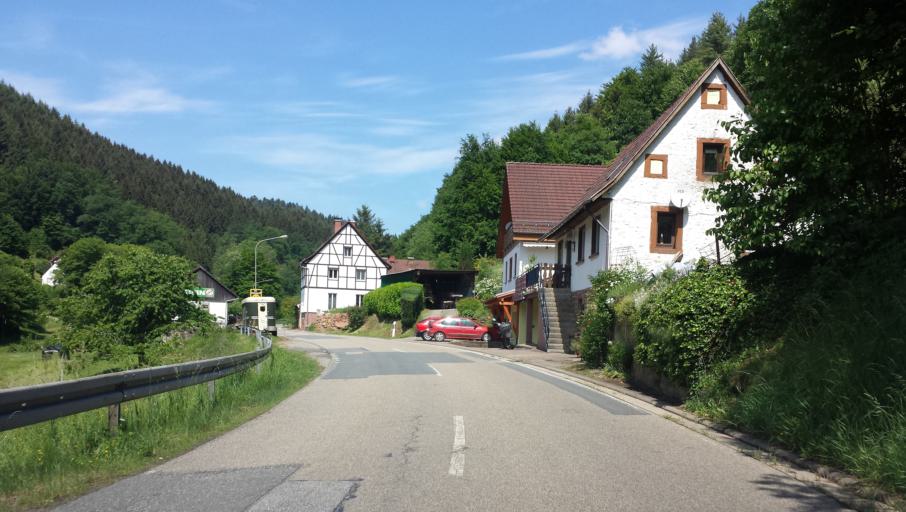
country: DE
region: Hesse
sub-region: Regierungsbezirk Darmstadt
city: Rothenberg
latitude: 49.5432
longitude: 8.9054
